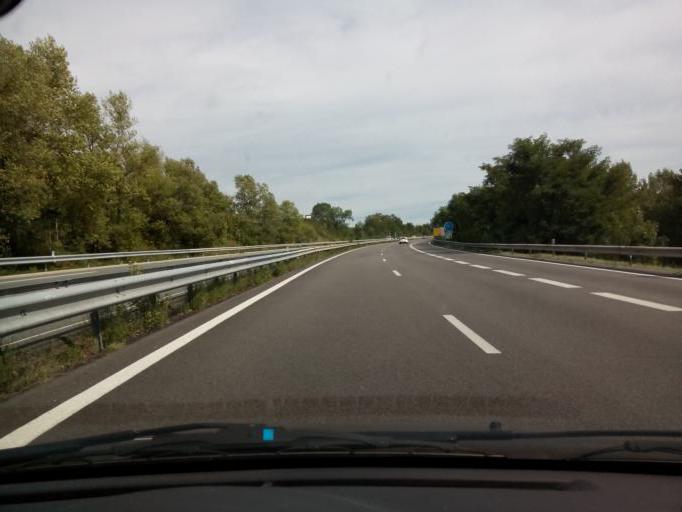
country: FR
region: Rhone-Alpes
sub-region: Departement de l'Isere
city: Saint-Victor-de-Cessieu
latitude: 45.5425
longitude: 5.3853
